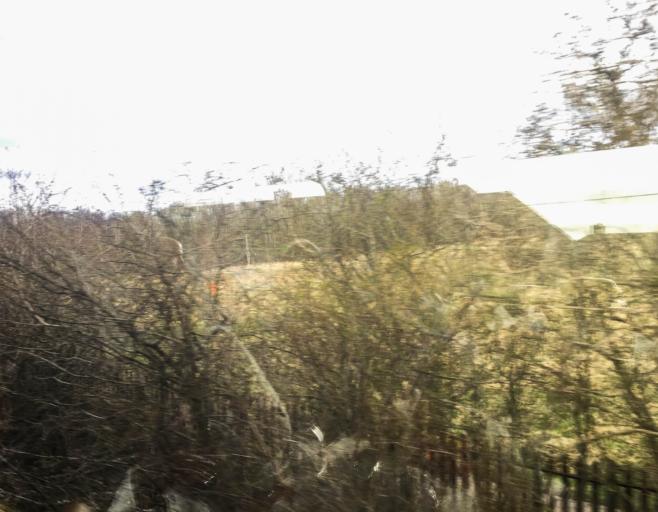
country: GB
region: Scotland
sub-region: North Lanarkshire
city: Wishaw
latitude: 55.7802
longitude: -3.9440
